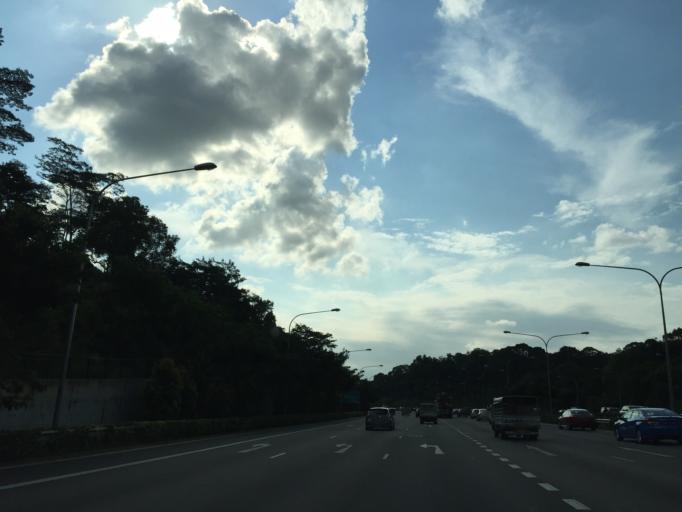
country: SG
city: Singapore
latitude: 1.3462
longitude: 103.7994
